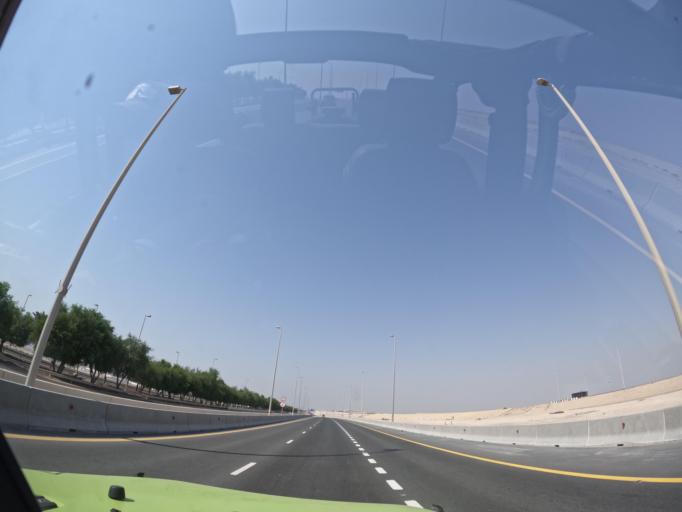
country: AE
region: Abu Dhabi
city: Abu Dhabi
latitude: 24.4208
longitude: 54.6777
